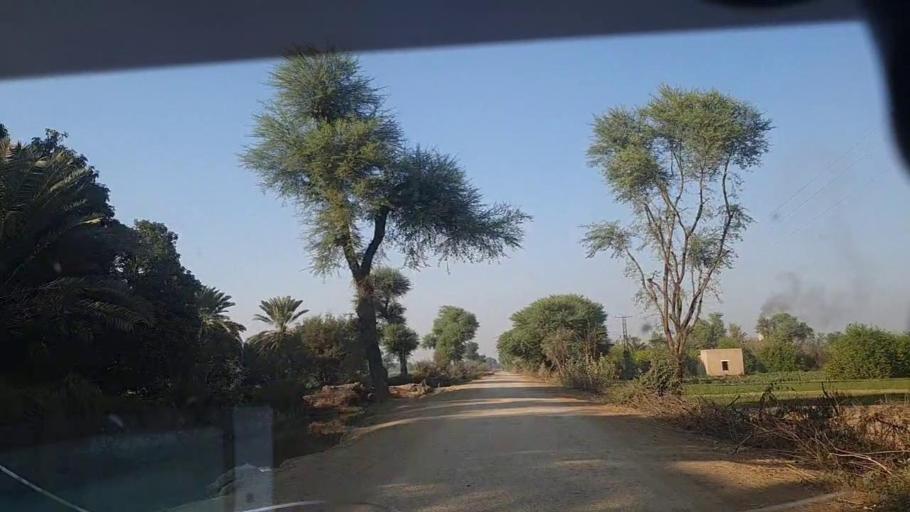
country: PK
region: Sindh
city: Sobhadero
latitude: 27.2592
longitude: 68.3508
